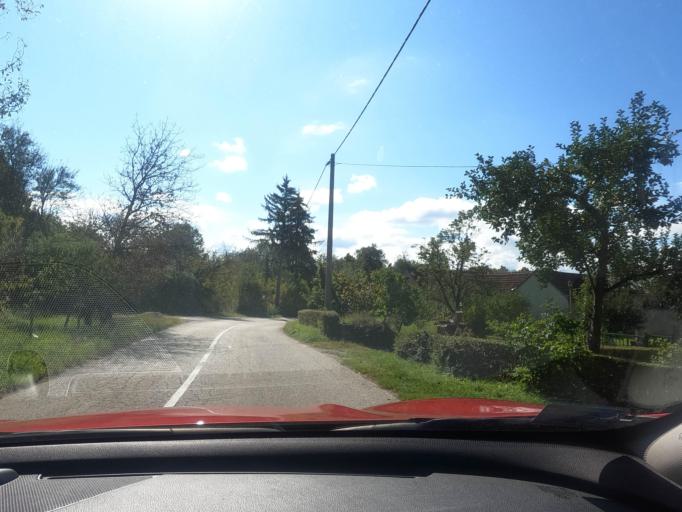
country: BA
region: Federation of Bosnia and Herzegovina
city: Vrnograc
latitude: 45.2600
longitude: 15.9496
